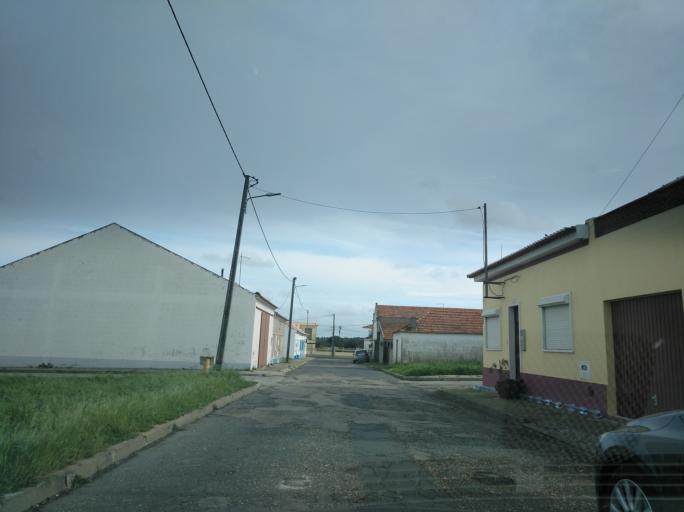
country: PT
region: Setubal
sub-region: Grandola
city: Grandola
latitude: 38.1905
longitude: -8.5540
